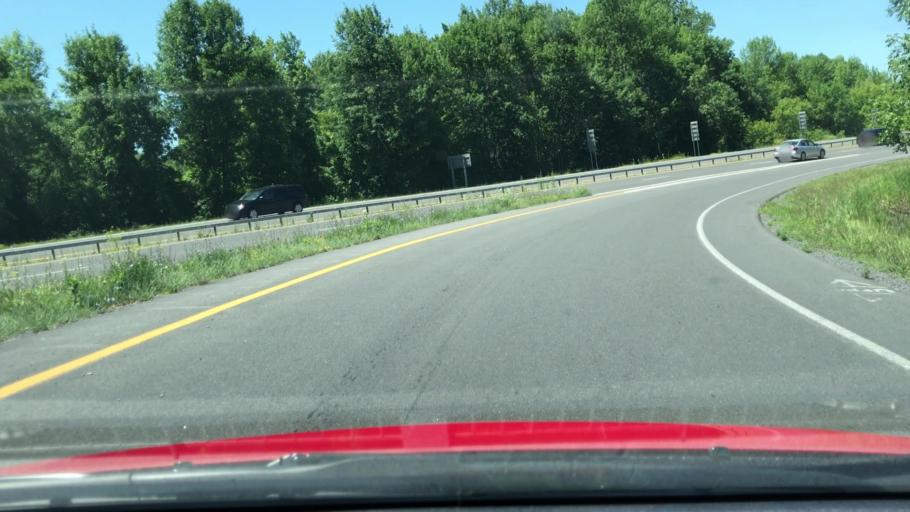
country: US
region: New York
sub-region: Clinton County
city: Plattsburgh
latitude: 44.7259
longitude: -73.4369
